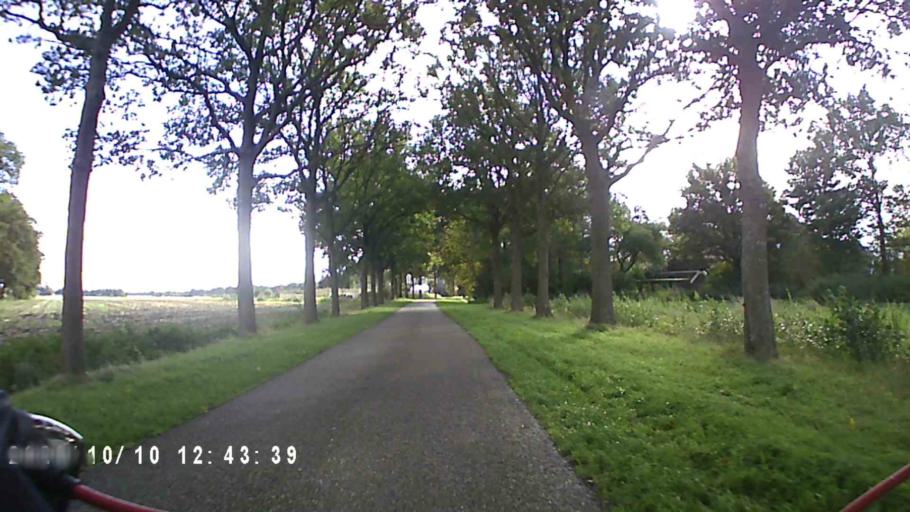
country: NL
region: Friesland
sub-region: Gemeente Weststellingwerf
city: Noordwolde
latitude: 52.9310
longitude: 6.2224
